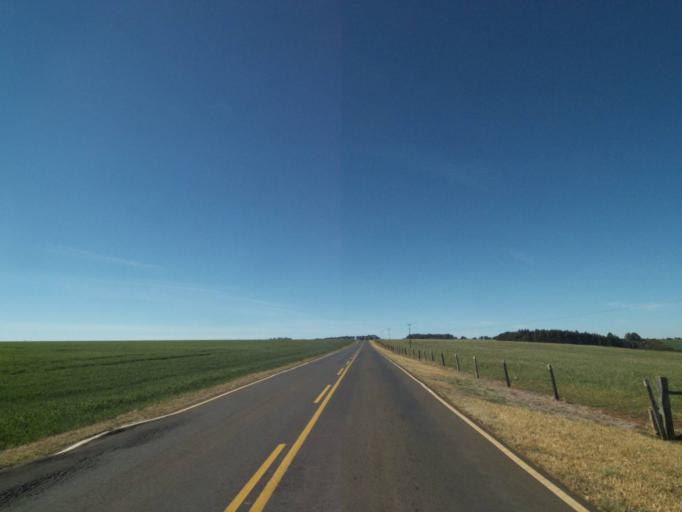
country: BR
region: Parana
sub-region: Tibagi
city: Tibagi
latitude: -24.5430
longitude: -50.3038
